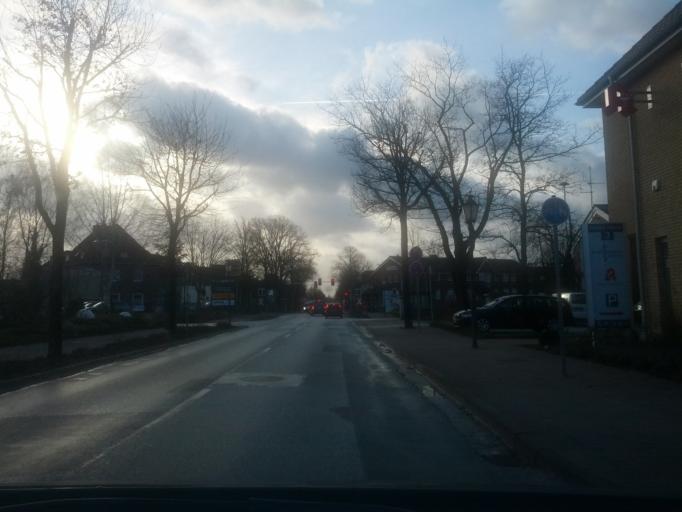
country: DE
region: Lower Saxony
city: Sittensen
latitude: 53.2835
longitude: 9.5059
